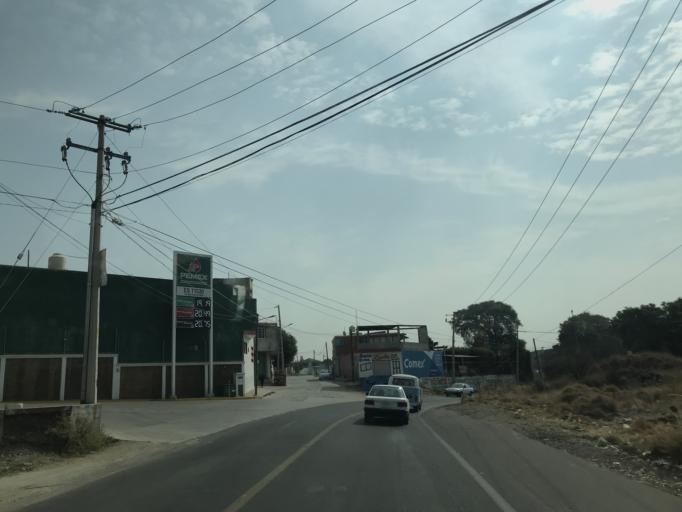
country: MX
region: Tlaxcala
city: Tenancingo
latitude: 19.1521
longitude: -98.2090
